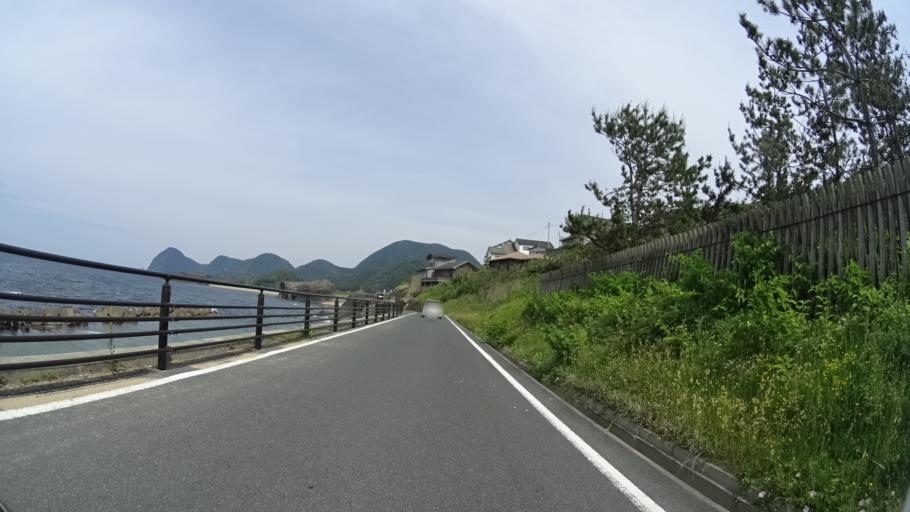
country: JP
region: Kyoto
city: Miyazu
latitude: 35.7412
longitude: 135.0969
